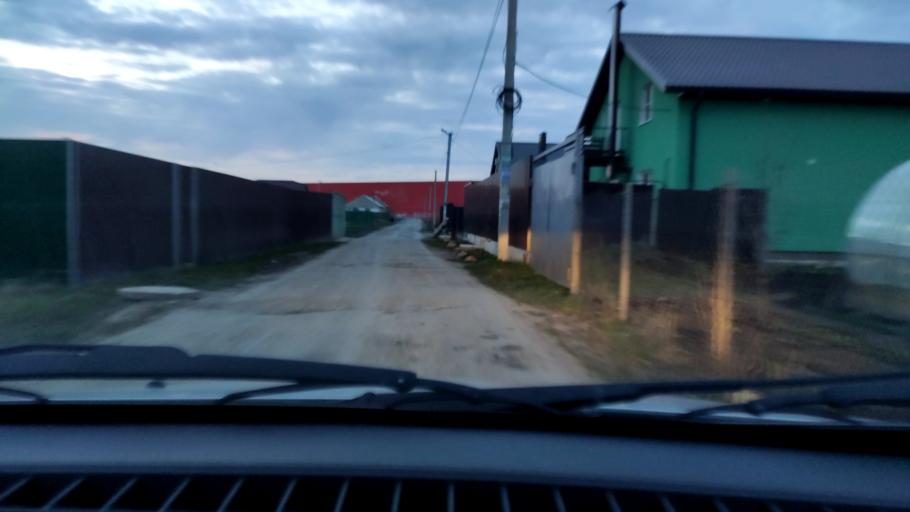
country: RU
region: Voronezj
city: Podgornoye
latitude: 51.7978
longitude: 39.2149
